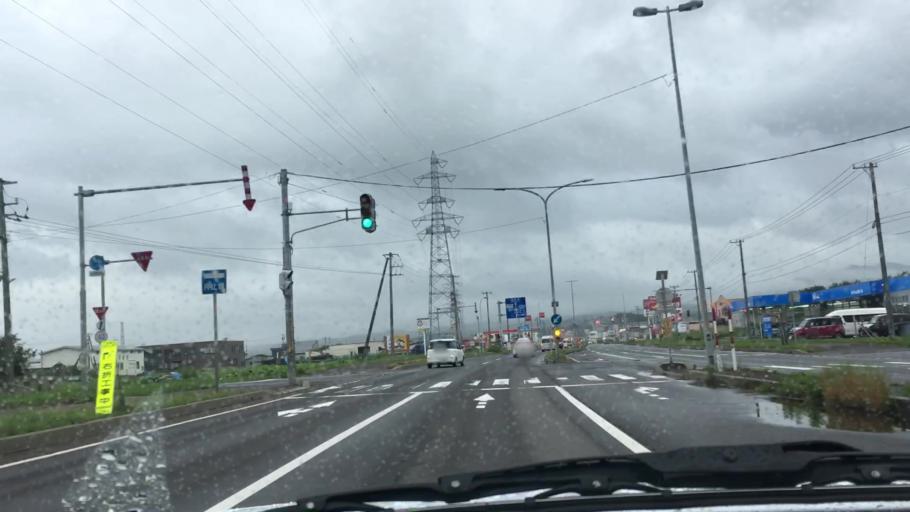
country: JP
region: Hokkaido
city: Nanae
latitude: 42.2540
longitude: 140.2832
